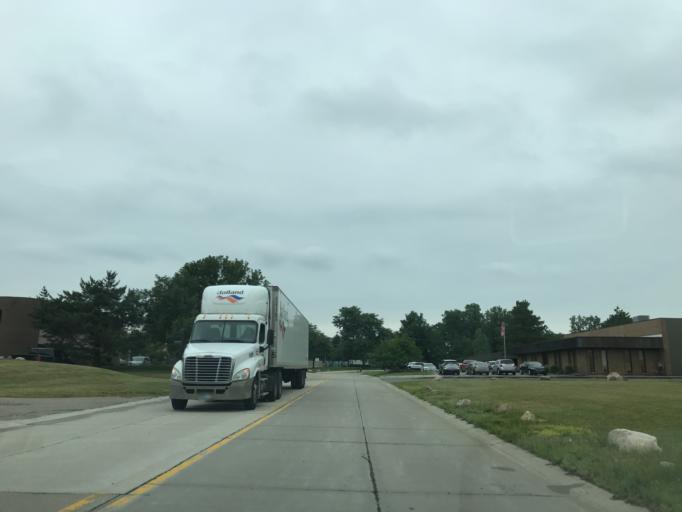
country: US
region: Michigan
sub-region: Oakland County
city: Farmington
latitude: 42.4717
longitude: -83.3916
